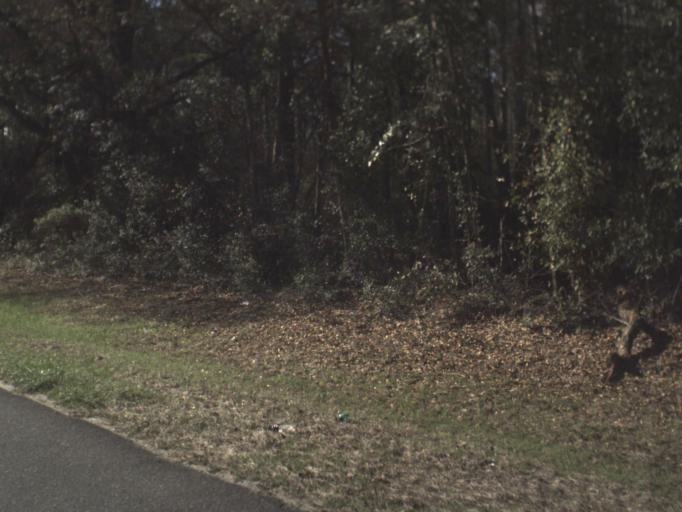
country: US
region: Florida
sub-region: Jackson County
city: Malone
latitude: 30.9263
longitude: -85.1623
